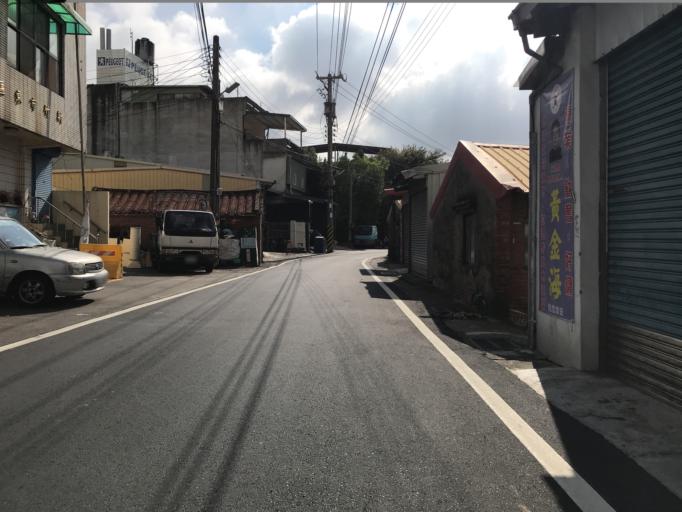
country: TW
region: Taiwan
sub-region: Hsinchu
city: Zhubei
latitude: 24.8115
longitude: 121.0018
